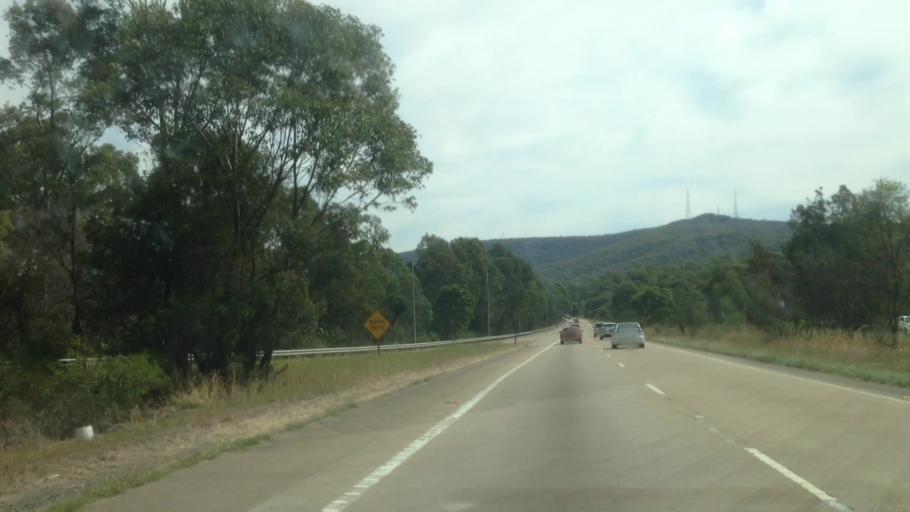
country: AU
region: New South Wales
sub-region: Lake Macquarie Shire
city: Holmesville
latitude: -32.8956
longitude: 151.5838
